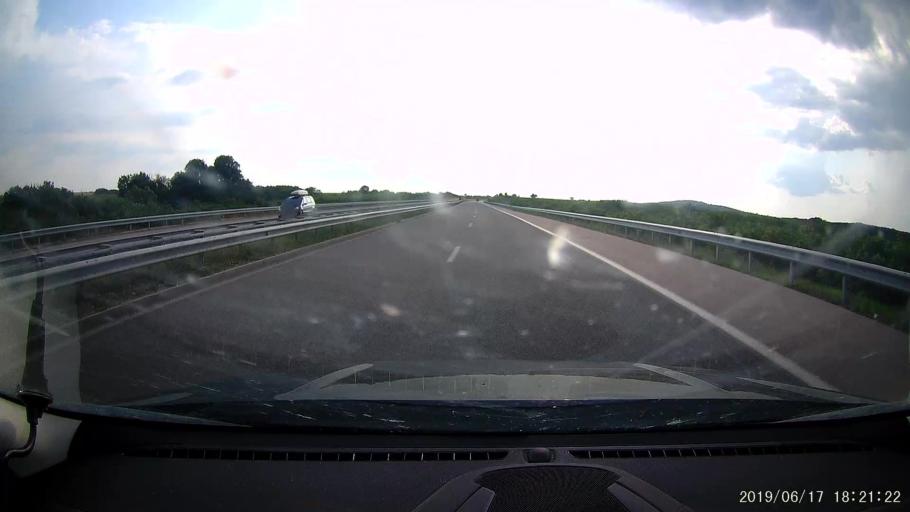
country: BG
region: Khaskovo
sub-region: Obshtina Simeonovgrad
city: Simeonovgrad
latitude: 41.9675
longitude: 25.7857
